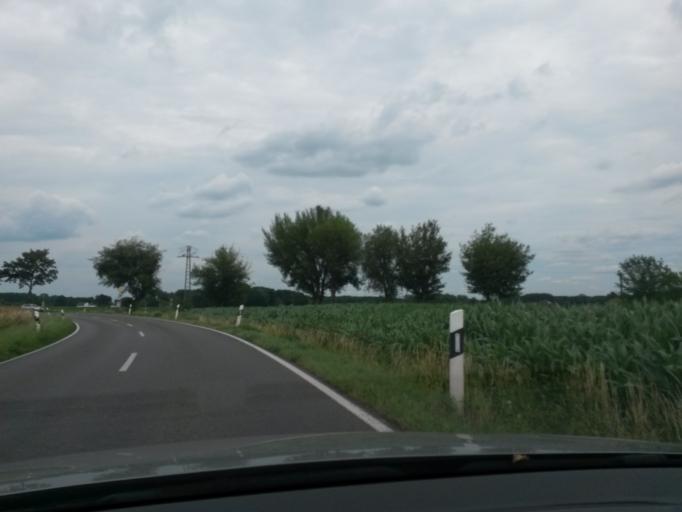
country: DE
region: North Rhine-Westphalia
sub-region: Regierungsbezirk Dusseldorf
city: Viersen
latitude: 51.3077
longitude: 6.3915
